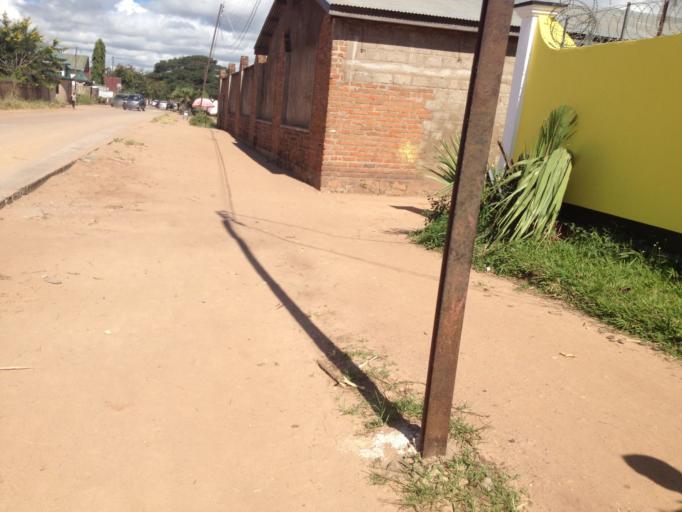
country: CD
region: Katanga
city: Kalemie
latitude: -5.9117
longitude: 29.2077
